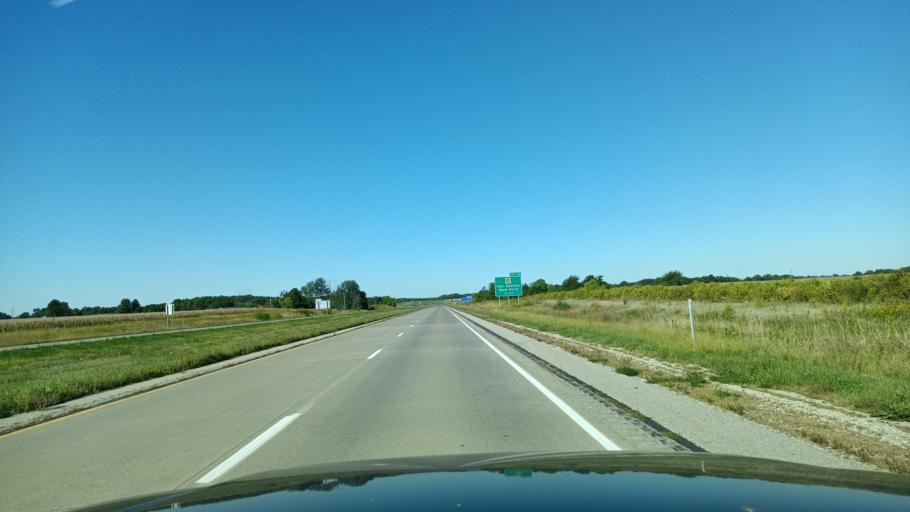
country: US
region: Iowa
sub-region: Lee County
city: Fort Madison
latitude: 40.6706
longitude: -91.3393
